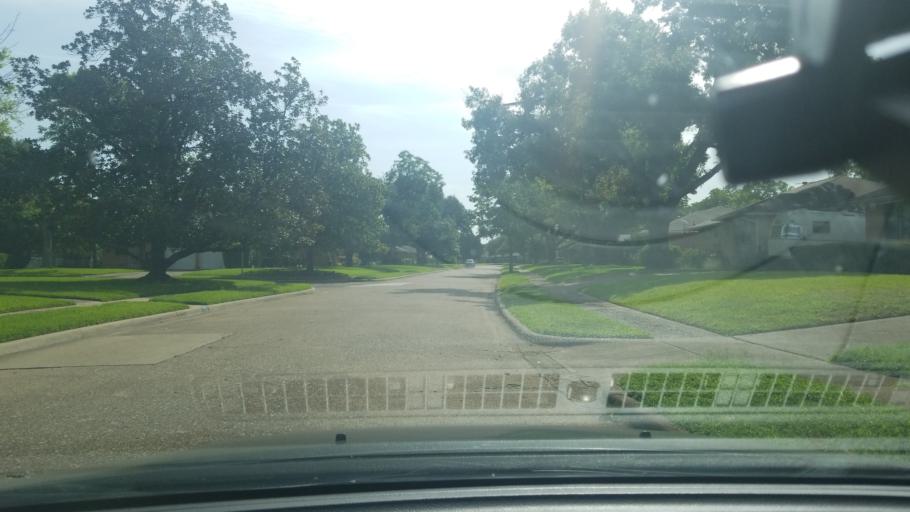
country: US
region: Texas
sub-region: Dallas County
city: Highland Park
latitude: 32.8058
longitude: -96.7050
